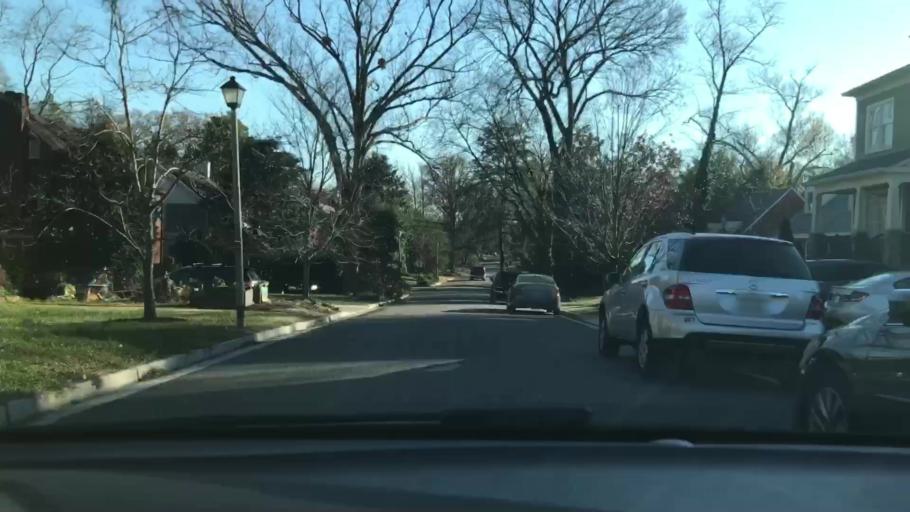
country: US
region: Virginia
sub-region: Arlington County
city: Arlington
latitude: 38.8784
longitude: -77.1014
